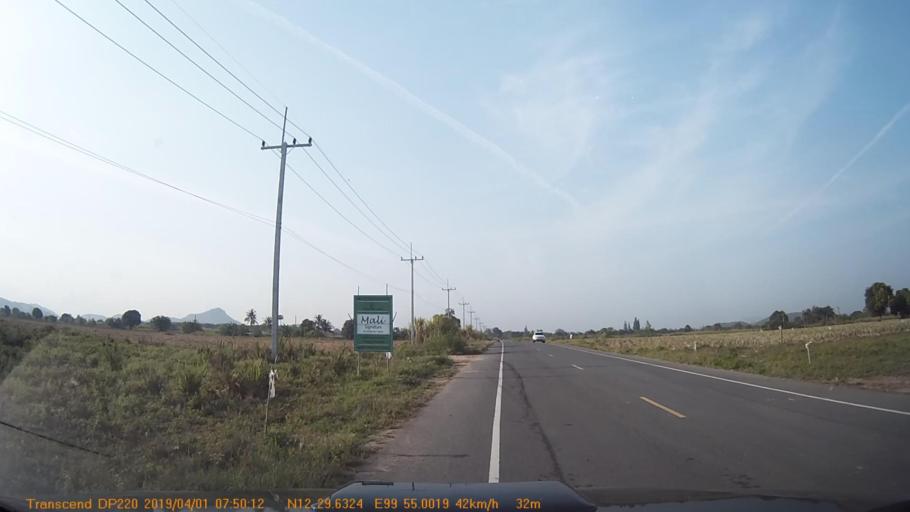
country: TH
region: Prachuap Khiri Khan
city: Hua Hin
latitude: 12.4939
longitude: 99.9167
